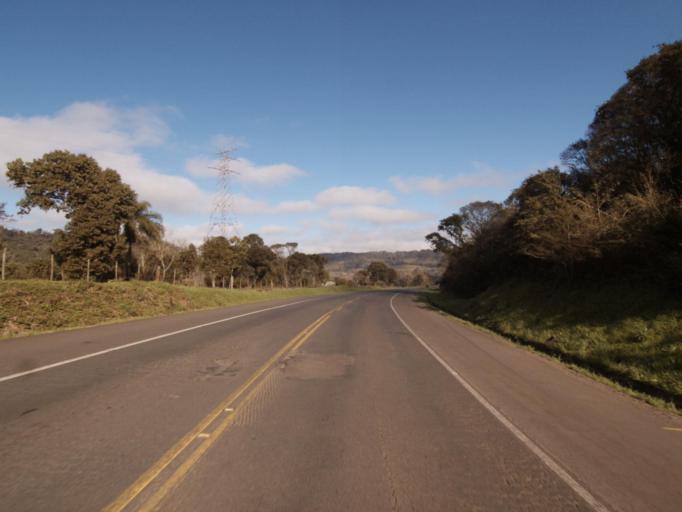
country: BR
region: Rio Grande do Sul
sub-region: Frederico Westphalen
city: Frederico Westphalen
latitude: -27.0656
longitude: -53.2225
